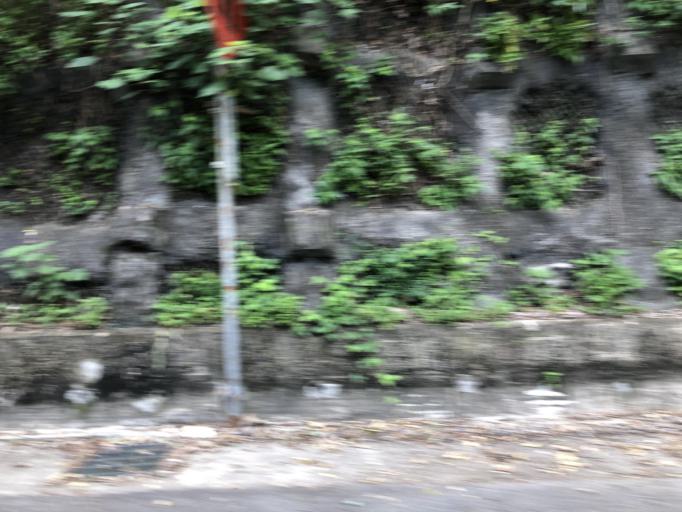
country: TW
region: Taiwan
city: Daxi
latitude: 24.6788
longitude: 121.3830
